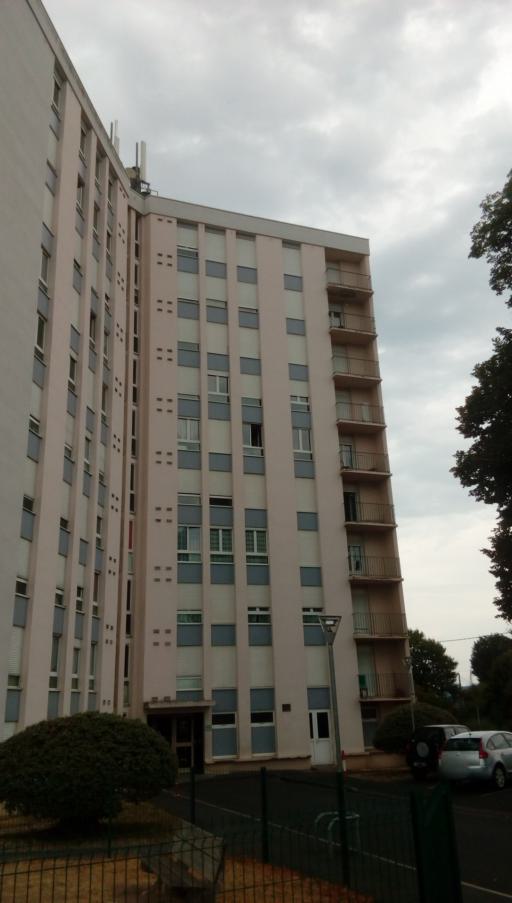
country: FR
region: Limousin
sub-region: Departement de la Creuse
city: Gueret
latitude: 46.1780
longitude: 1.8641
